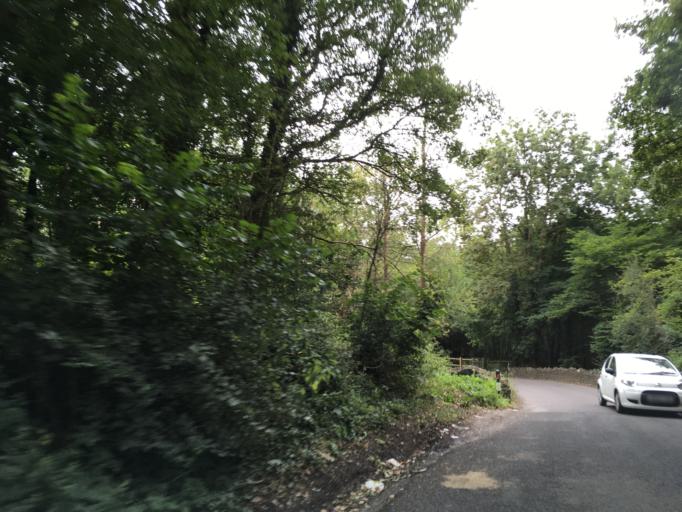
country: GB
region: England
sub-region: South Gloucestershire
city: Siston
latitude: 51.4728
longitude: -2.4520
